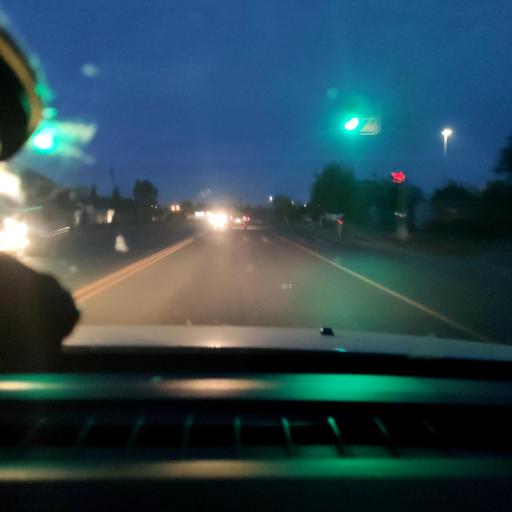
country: RU
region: Samara
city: Samara
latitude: 53.1302
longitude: 50.0936
